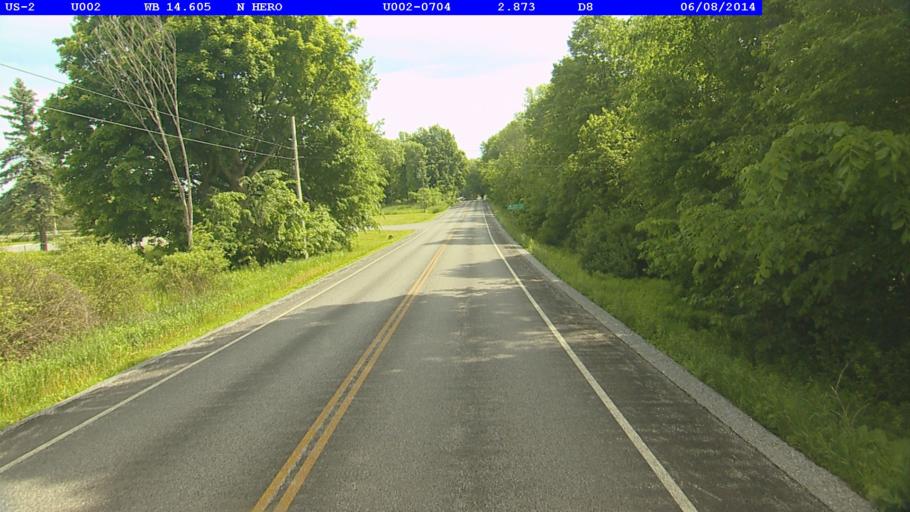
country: US
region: Vermont
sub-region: Grand Isle County
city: North Hero
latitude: 44.8498
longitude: -73.2631
